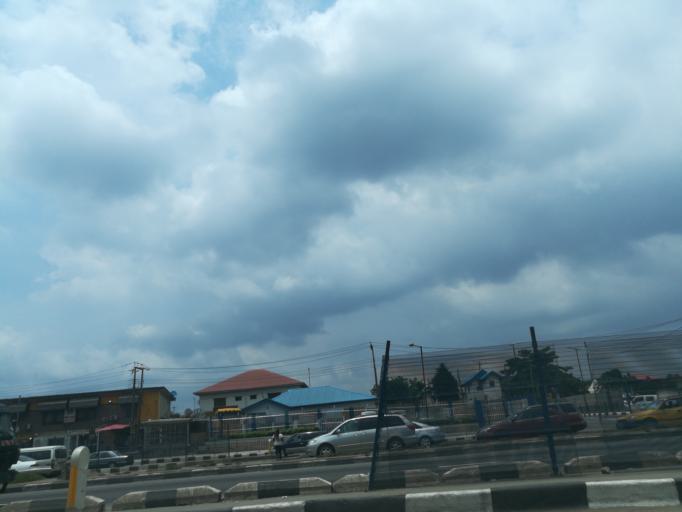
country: NG
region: Lagos
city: Ojota
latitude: 6.5745
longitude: 3.3695
